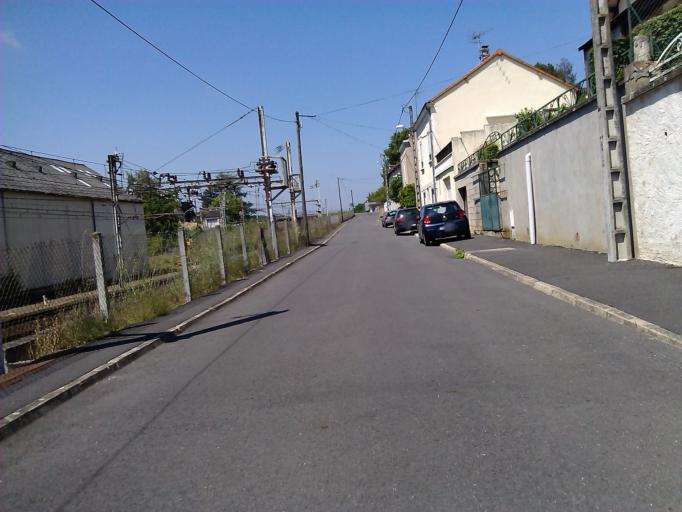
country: FR
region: Centre
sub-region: Departement de l'Indre
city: Saint-Marcel
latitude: 46.5964
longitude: 1.5132
